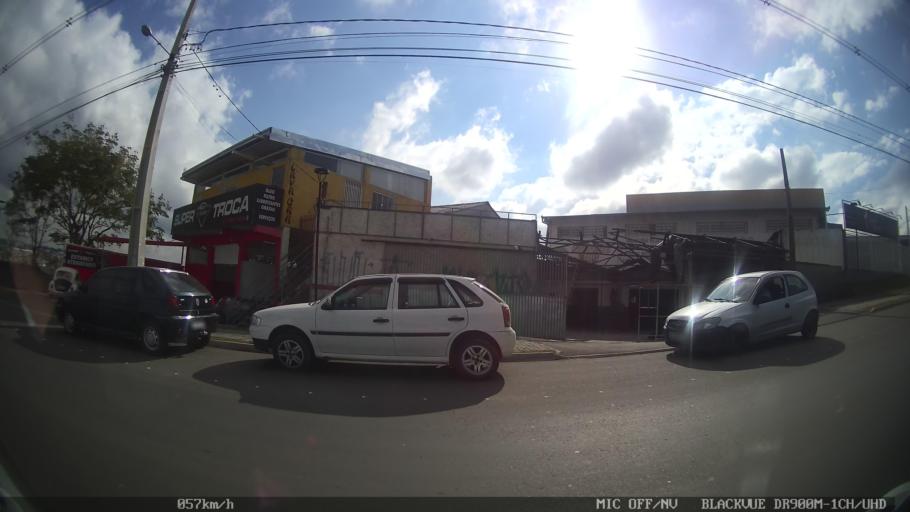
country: BR
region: Parana
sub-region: Pinhais
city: Pinhais
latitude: -25.3807
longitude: -49.1844
